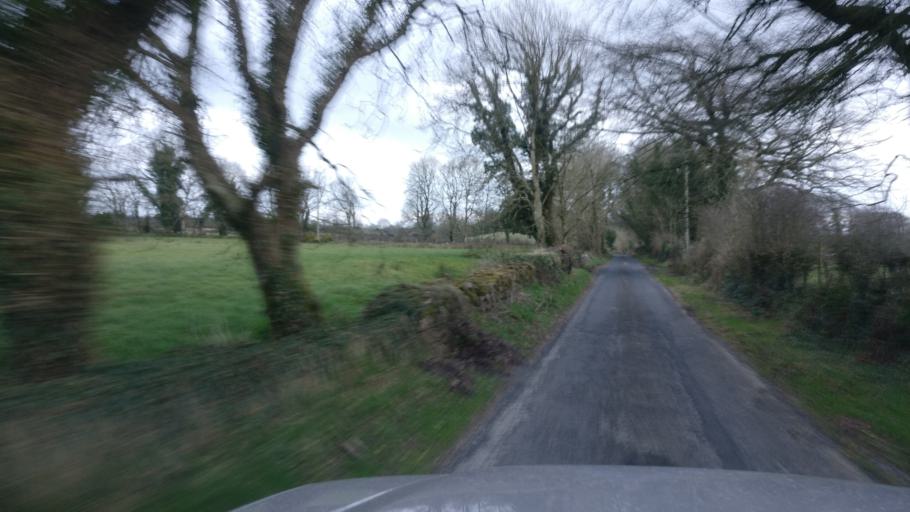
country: IE
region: Connaught
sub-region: County Galway
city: Loughrea
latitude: 53.2628
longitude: -8.4577
